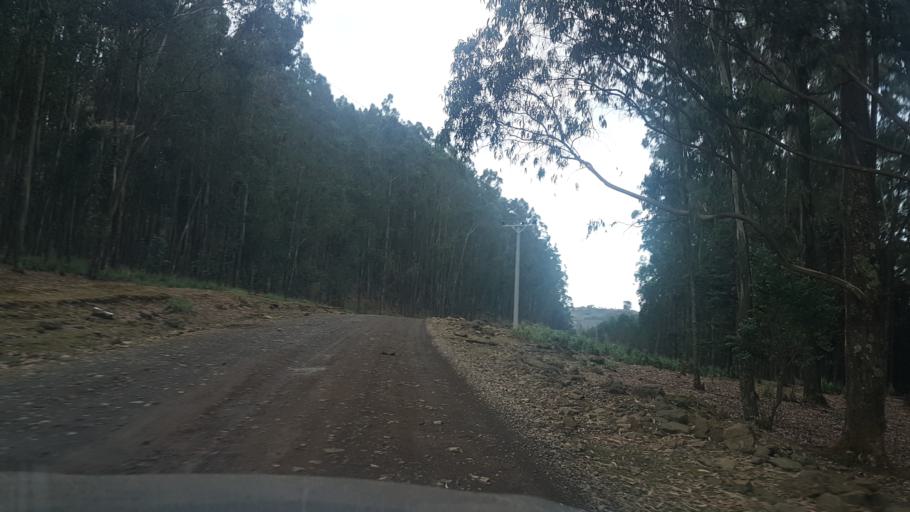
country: ET
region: Amhara
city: Finote Selam
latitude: 10.7938
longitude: 37.6637
